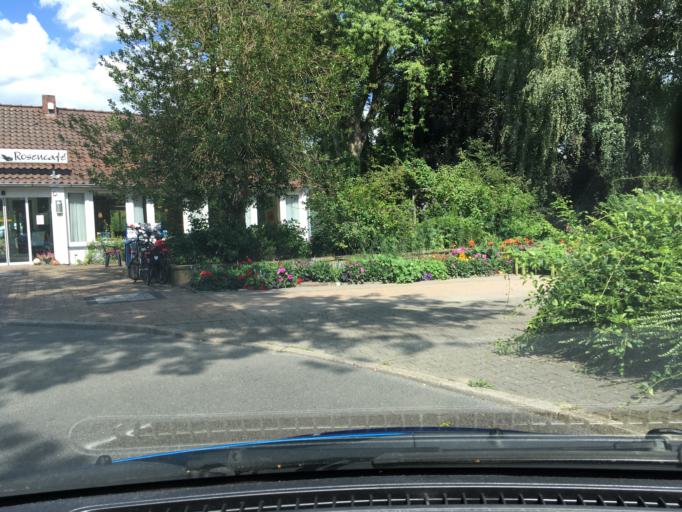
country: DE
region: Lower Saxony
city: Bad Bevensen
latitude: 53.0826
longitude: 10.5822
